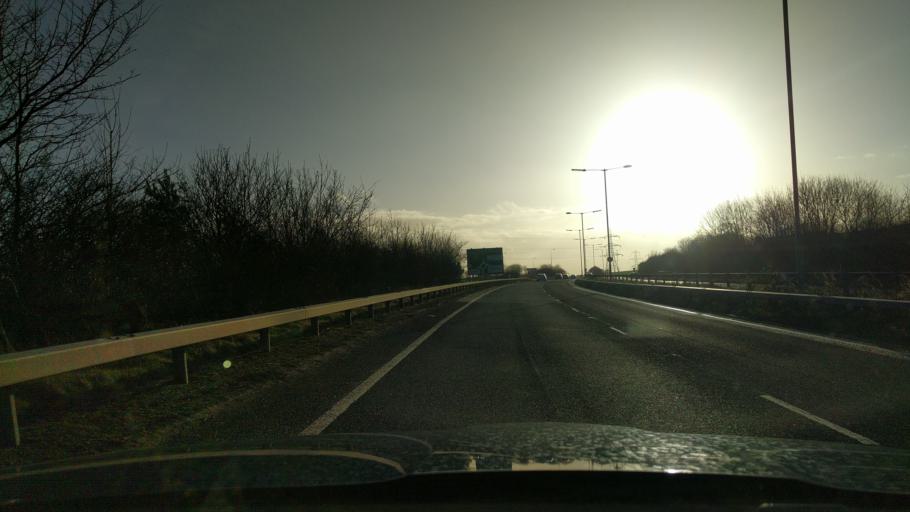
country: GB
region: England
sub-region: Northumberland
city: Newbiggin-by-the-Sea
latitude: 55.1745
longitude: -1.5303
